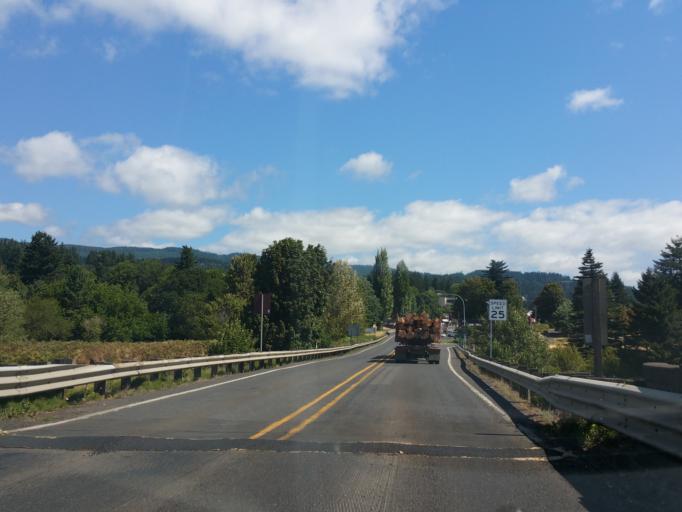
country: US
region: Washington
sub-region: Skamania County
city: Stevenson
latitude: 45.6881
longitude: -121.8910
